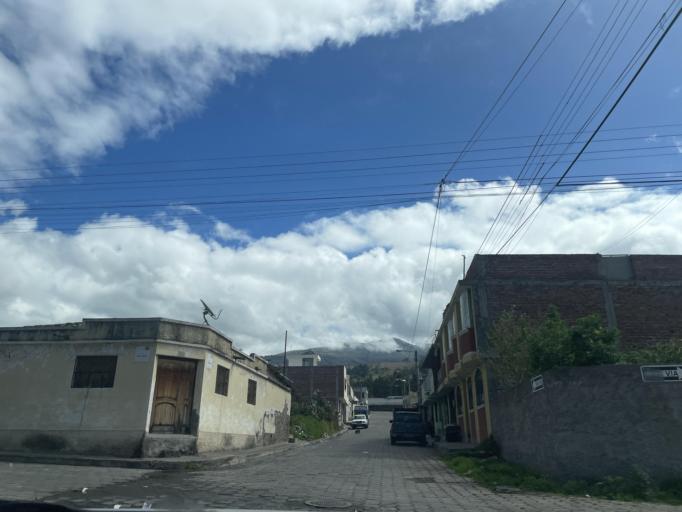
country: EC
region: Chimborazo
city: Guano
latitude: -1.6043
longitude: -78.6436
